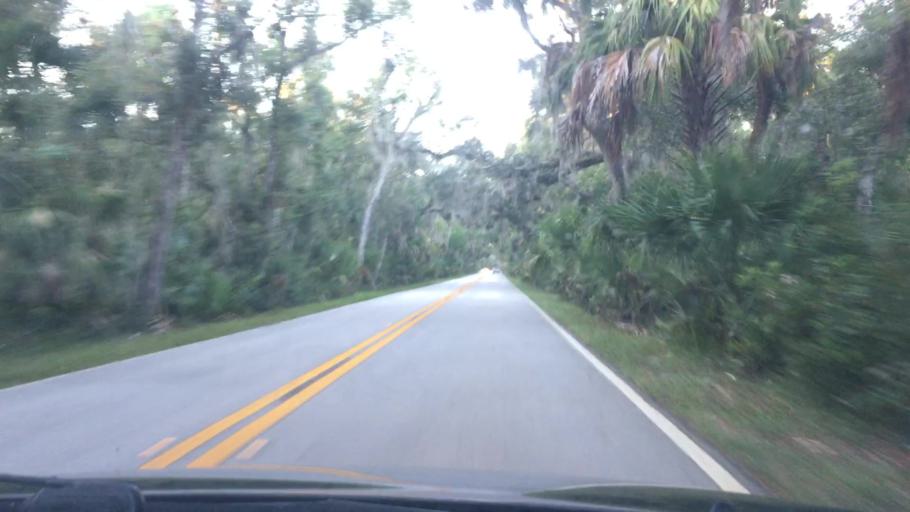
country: US
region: Florida
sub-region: Volusia County
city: Ormond-by-the-Sea
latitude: 29.3366
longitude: -81.0818
